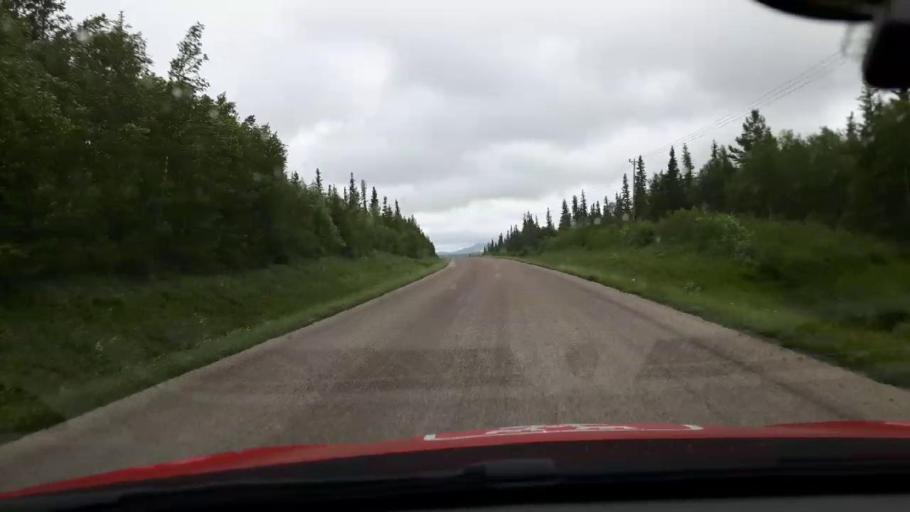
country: NO
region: Nord-Trondelag
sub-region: Meraker
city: Meraker
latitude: 63.2790
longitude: 12.3546
